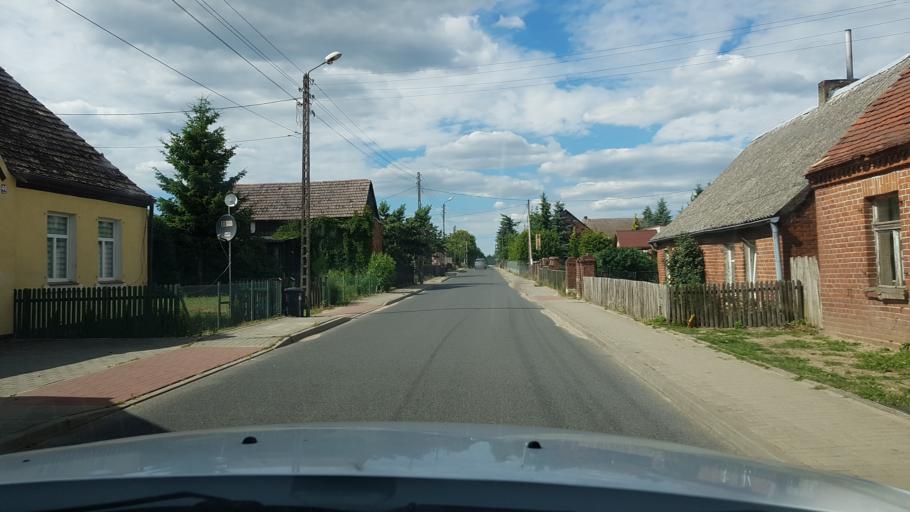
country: PL
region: West Pomeranian Voivodeship
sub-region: Powiat drawski
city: Wierzchowo
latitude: 53.4405
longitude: 16.0737
